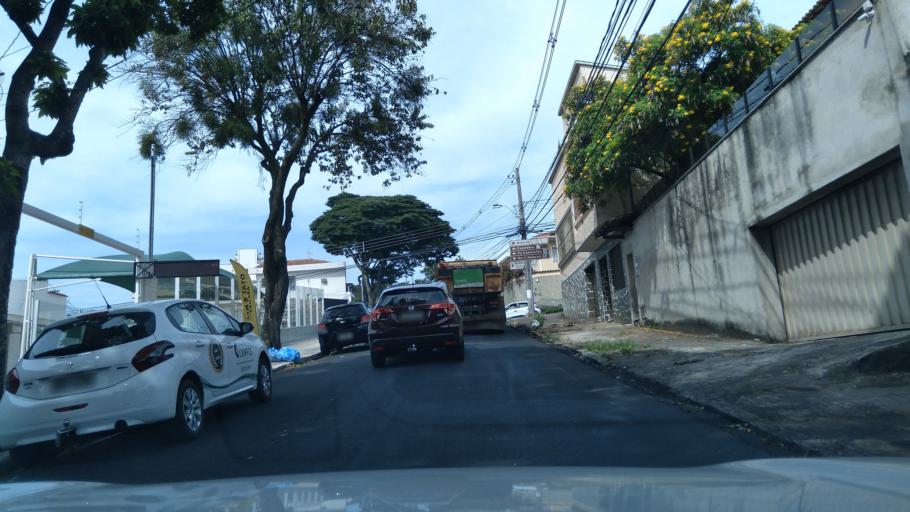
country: BR
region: Minas Gerais
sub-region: Belo Horizonte
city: Belo Horizonte
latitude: -19.9078
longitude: -43.9648
